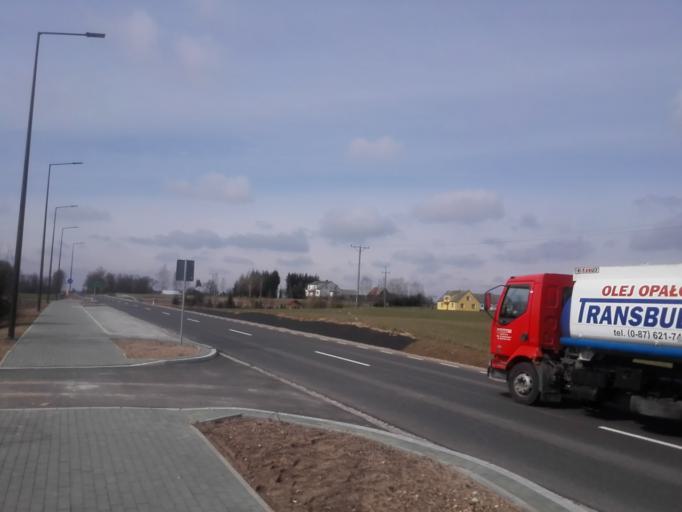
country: PL
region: Podlasie
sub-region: Powiat sejnenski
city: Sejny
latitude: 54.1095
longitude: 23.3293
